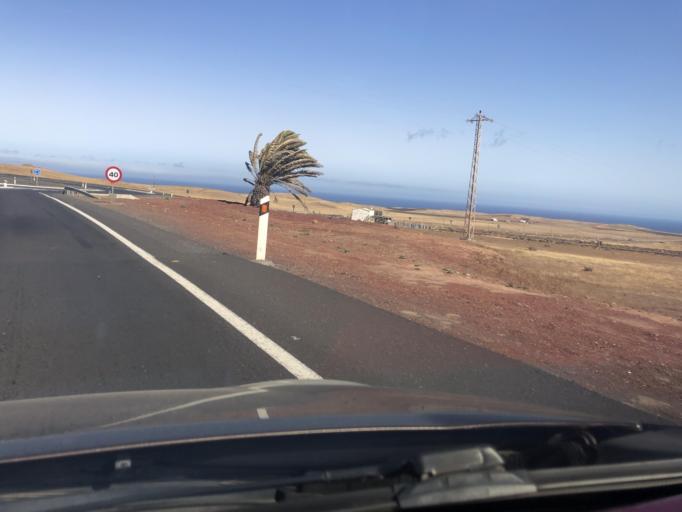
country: ES
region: Canary Islands
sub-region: Provincia de Las Palmas
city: Yaiza
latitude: 28.9369
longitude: -13.7315
